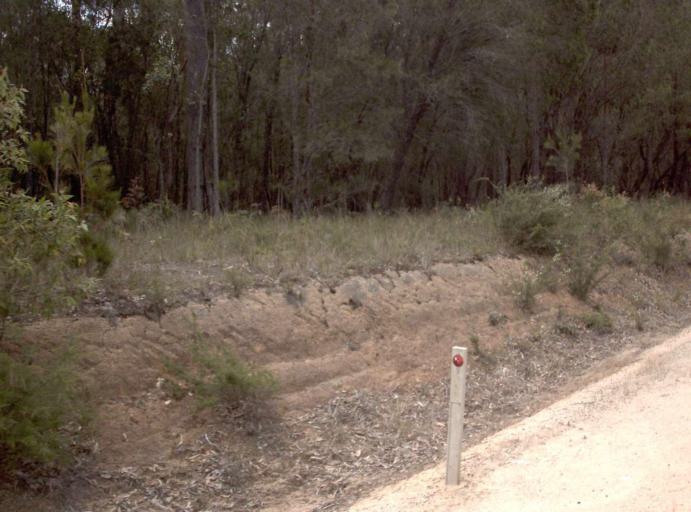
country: AU
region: New South Wales
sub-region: Bega Valley
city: Eden
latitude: -37.4257
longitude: 149.6453
